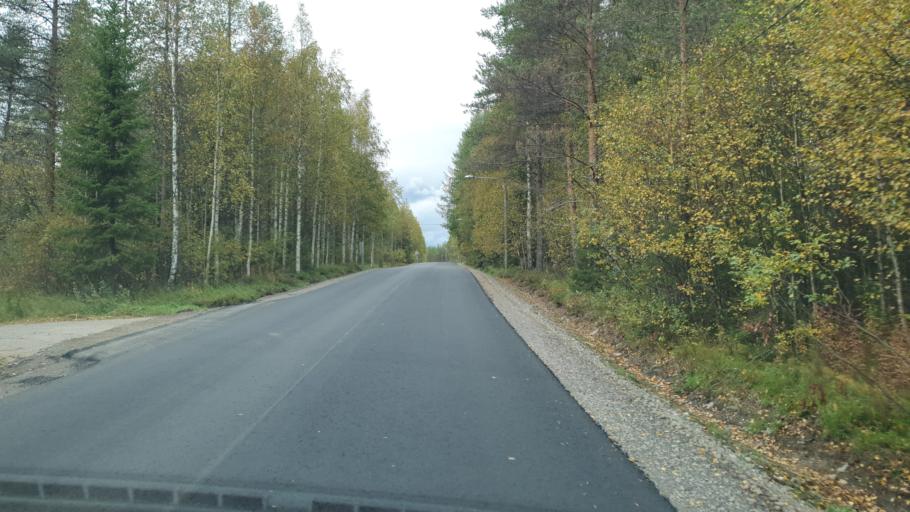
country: FI
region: Lapland
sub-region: Rovaniemi
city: Rovaniemi
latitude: 66.4214
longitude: 25.4057
